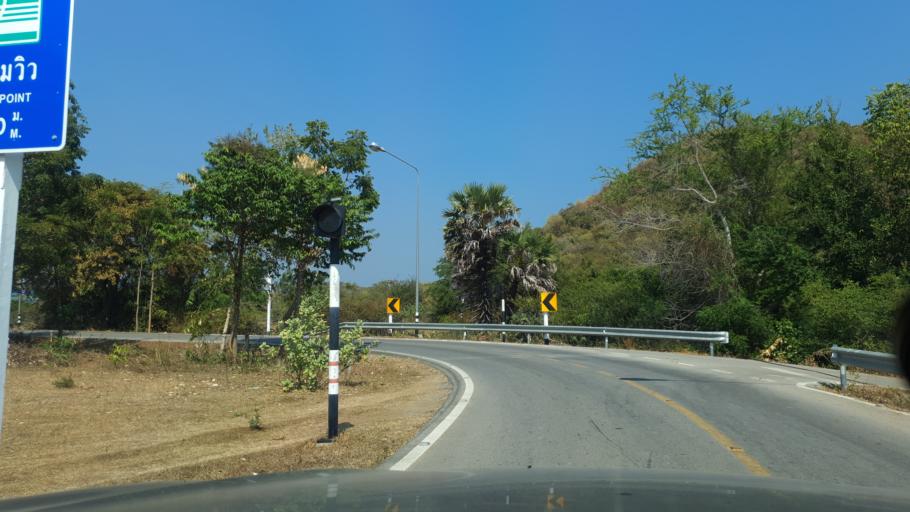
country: TH
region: Prachuap Khiri Khan
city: Sam Roi Yot
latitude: 12.2785
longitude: 99.9735
